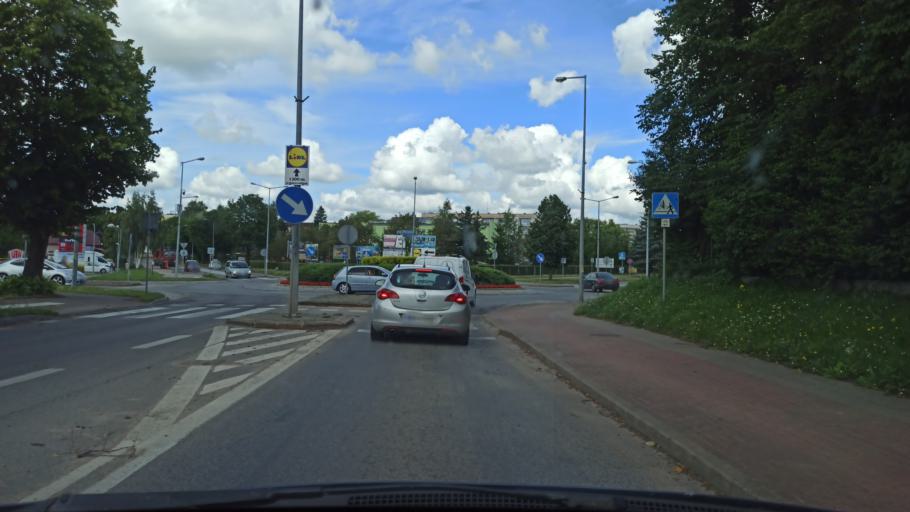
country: PL
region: Warmian-Masurian Voivodeship
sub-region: Powiat ostrodzki
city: Morag
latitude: 53.9071
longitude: 19.9364
